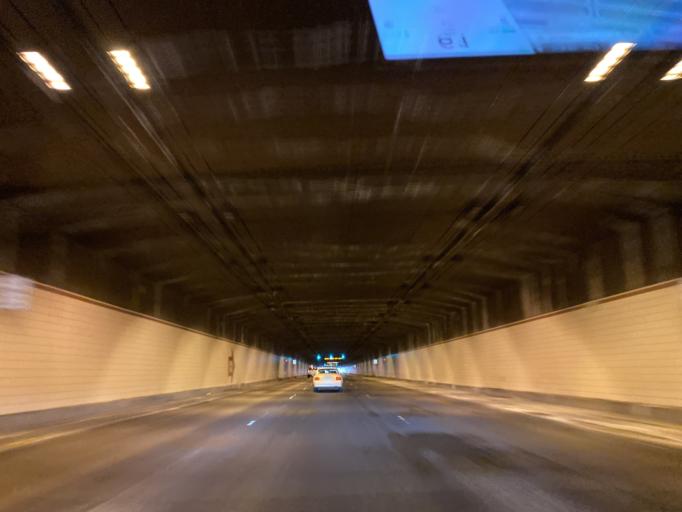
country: US
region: Nevada
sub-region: Clark County
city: Paradise
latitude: 36.0743
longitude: -115.1450
